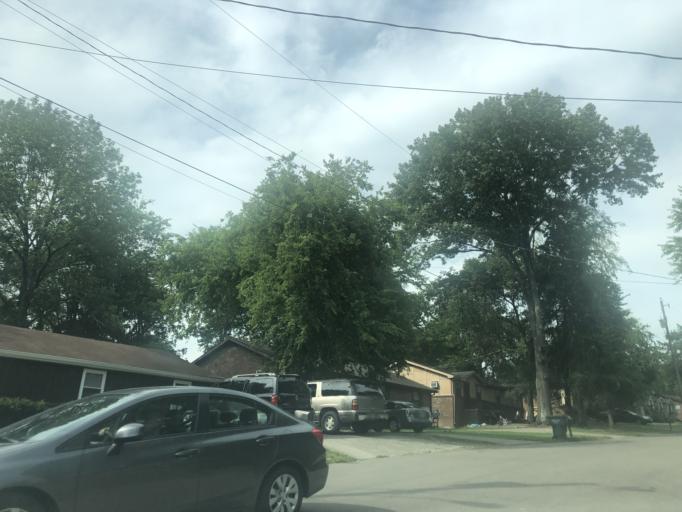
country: US
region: Tennessee
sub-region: Wilson County
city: Green Hill
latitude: 36.1750
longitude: -86.5895
